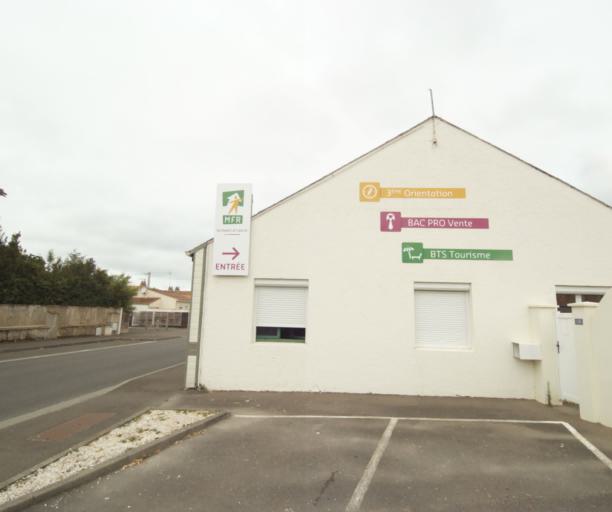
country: FR
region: Pays de la Loire
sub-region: Departement de la Vendee
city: Les Sables-d'Olonne
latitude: 46.4946
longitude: -1.7620
